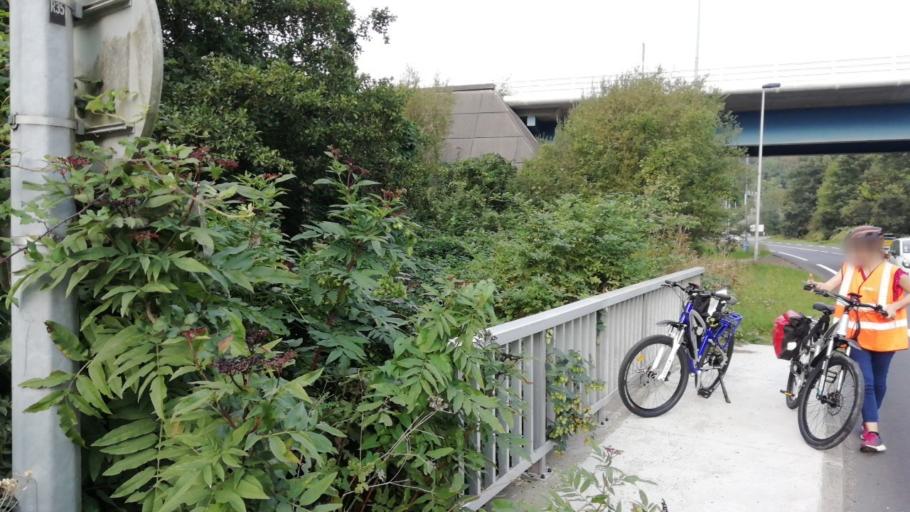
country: FR
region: Haute-Normandie
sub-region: Departement de la Seine-Maritime
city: Rogerville
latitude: 49.4965
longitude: 0.2714
